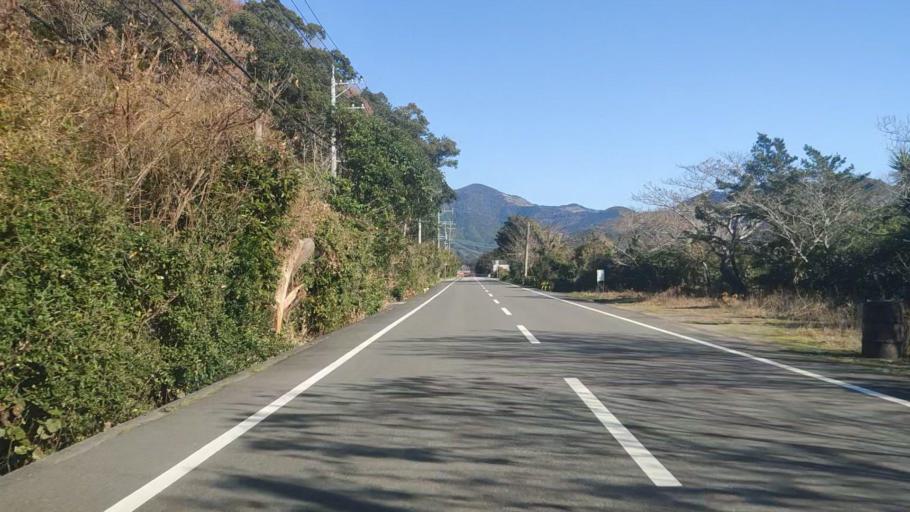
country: JP
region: Oita
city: Saiki
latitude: 32.7985
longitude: 131.8870
